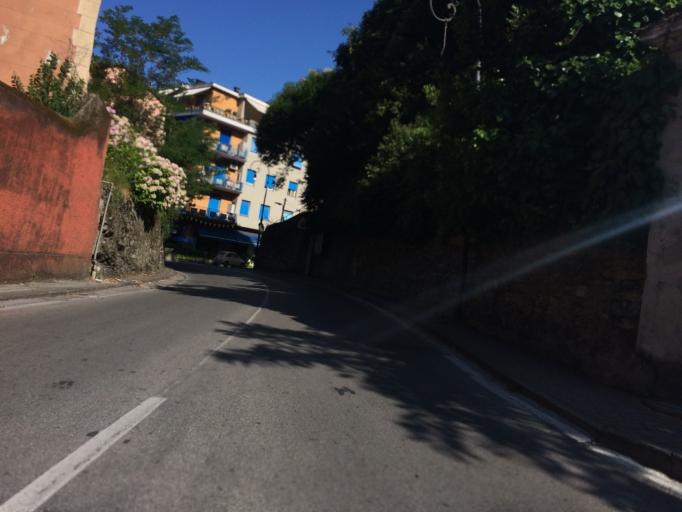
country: IT
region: Liguria
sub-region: Provincia di Genova
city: Rapallo
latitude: 44.3473
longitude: 9.2410
